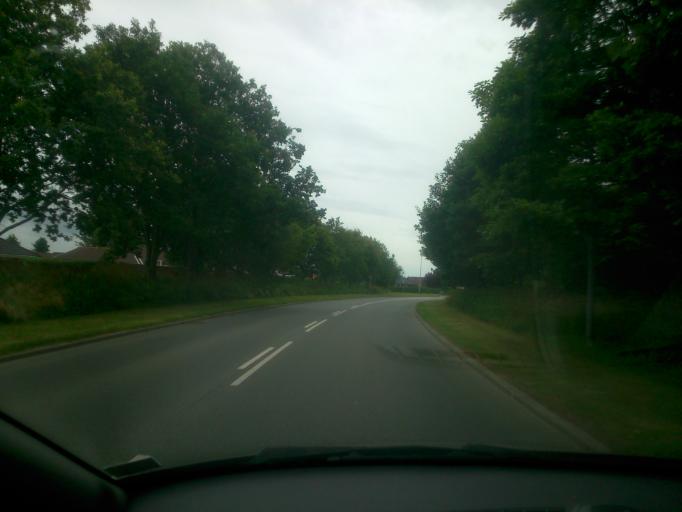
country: DK
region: South Denmark
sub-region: Esbjerg Kommune
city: Esbjerg
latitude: 55.5168
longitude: 8.4247
